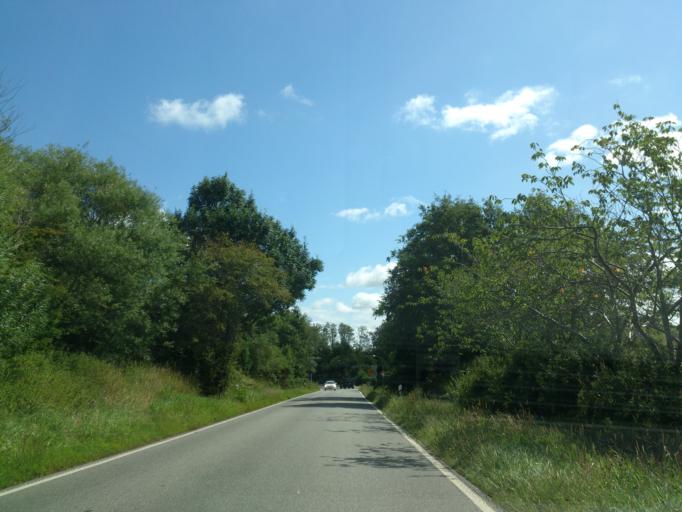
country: DE
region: Schleswig-Holstein
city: Tonning
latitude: 54.3072
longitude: 8.9285
